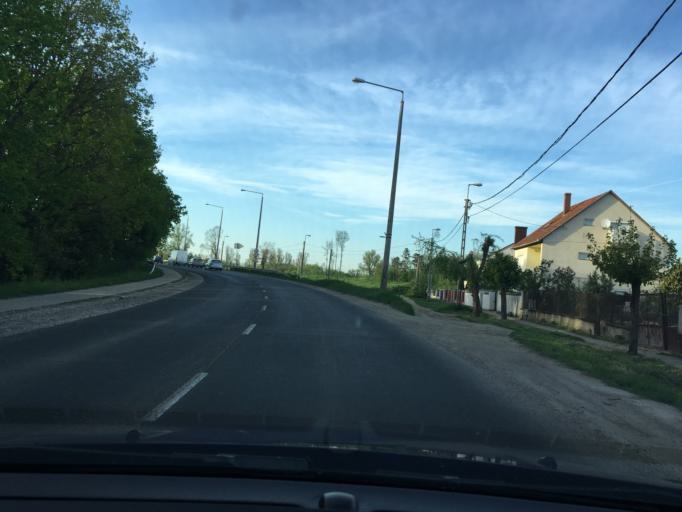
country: HU
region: Hajdu-Bihar
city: Berettyoujfalu
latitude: 47.2054
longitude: 21.5394
